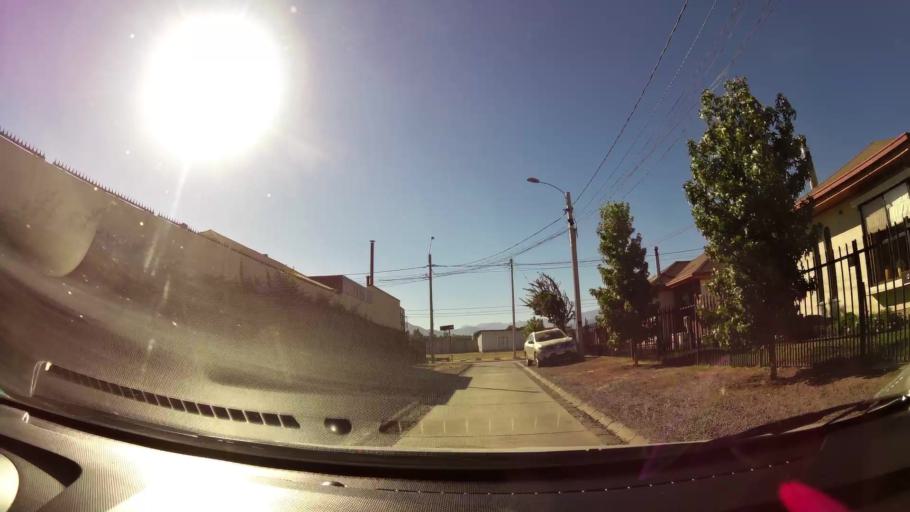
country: CL
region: O'Higgins
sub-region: Provincia de Cachapoal
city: Rancagua
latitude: -34.1960
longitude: -70.7194
